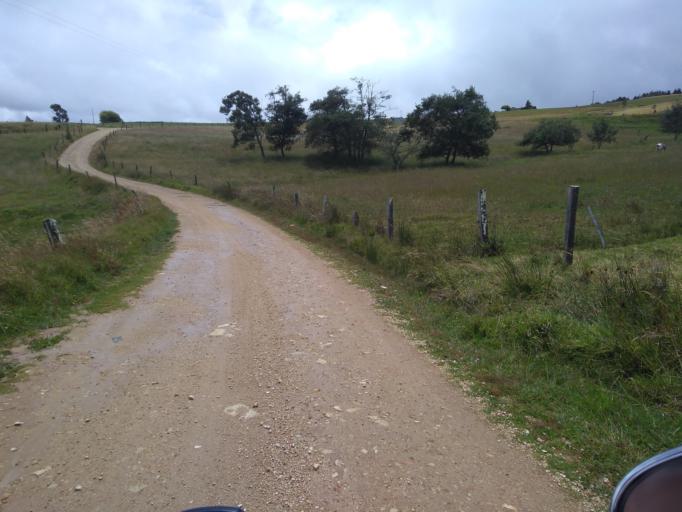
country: CO
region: Boyaca
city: Toca
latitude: 5.5871
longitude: -73.1400
